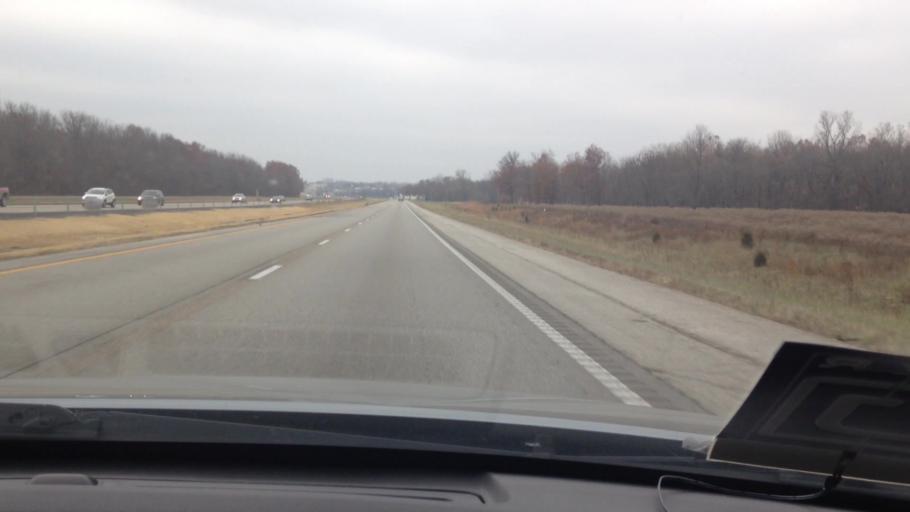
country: US
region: Missouri
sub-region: Cass County
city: Peculiar
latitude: 38.6918
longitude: -94.4276
